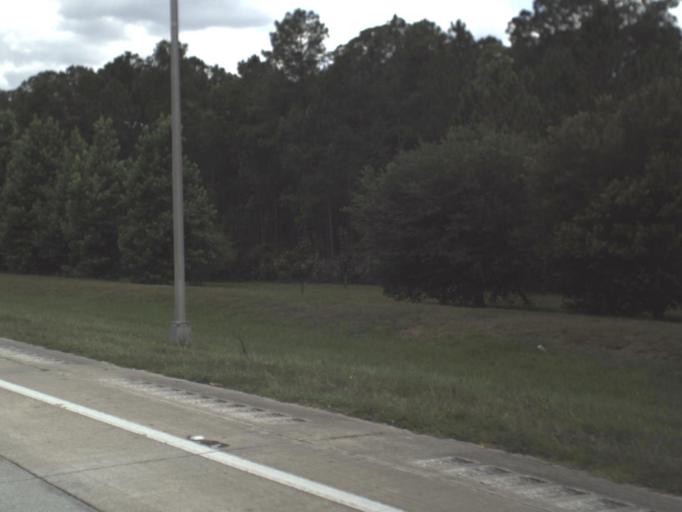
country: US
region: Florida
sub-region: Saint Johns County
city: Palm Valley
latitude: 30.2092
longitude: -81.5141
